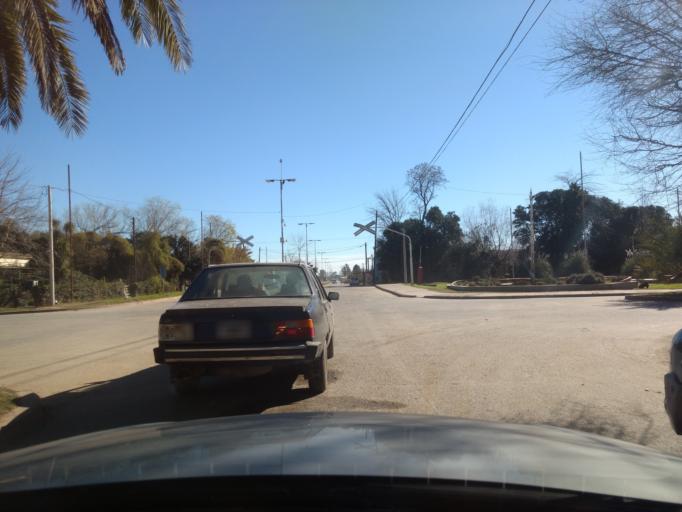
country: AR
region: Buenos Aires
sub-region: Partido de Navarro
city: Navarro
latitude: -34.9985
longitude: -59.2738
